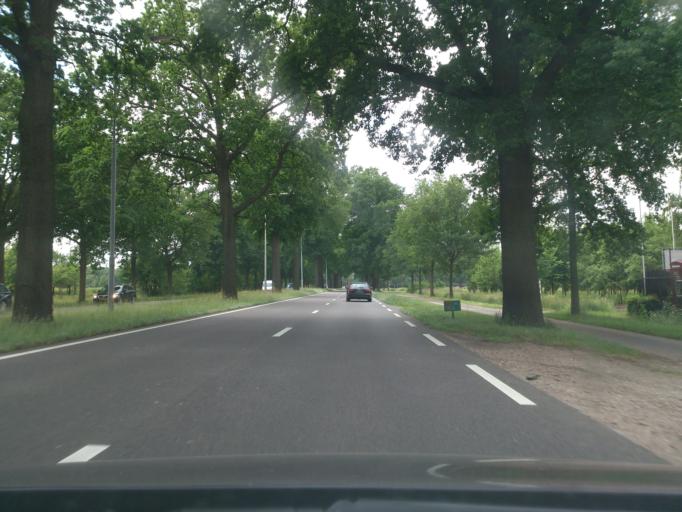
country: NL
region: North Brabant
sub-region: Gemeente Haaren
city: Haaren
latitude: 51.6215
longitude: 5.2210
